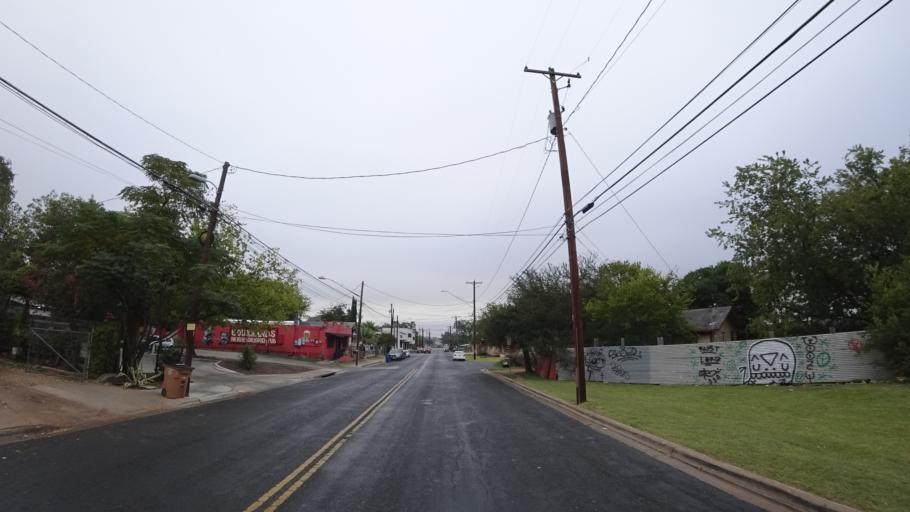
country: US
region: Texas
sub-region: Travis County
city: Austin
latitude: 30.2623
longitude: -97.7157
